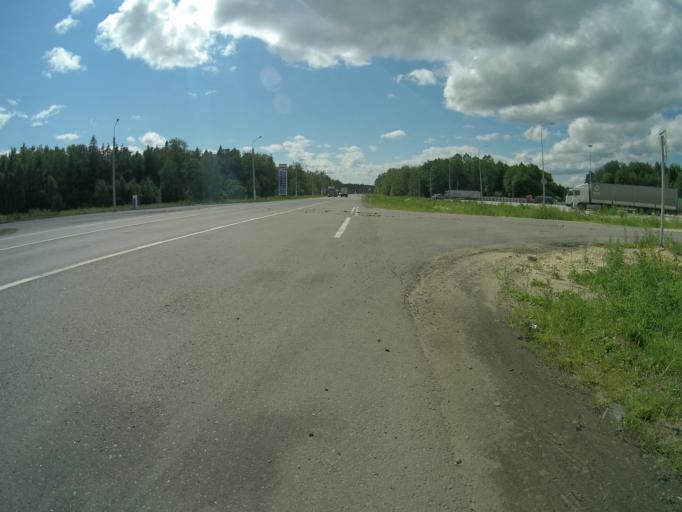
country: RU
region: Vladimir
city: Raduzhnyy
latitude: 56.0716
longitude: 40.2401
